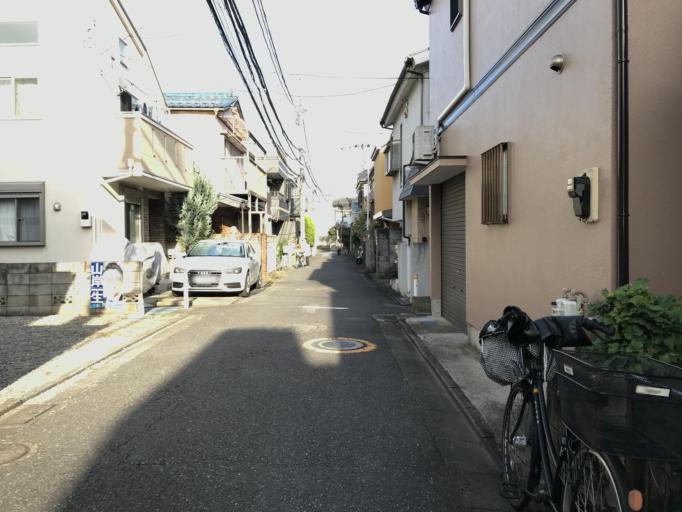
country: JP
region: Saitama
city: Wako
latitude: 35.7560
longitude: 139.5951
